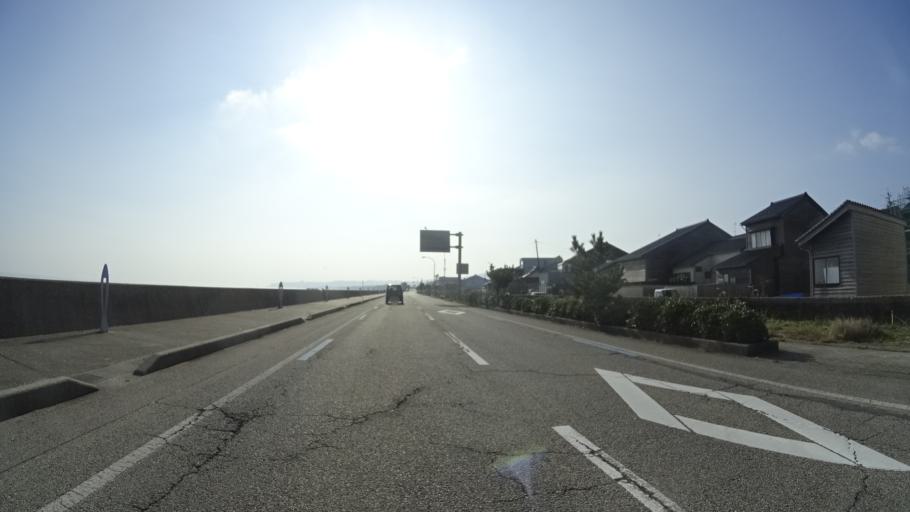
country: JP
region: Toyama
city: Himi
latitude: 36.8516
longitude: 136.9925
